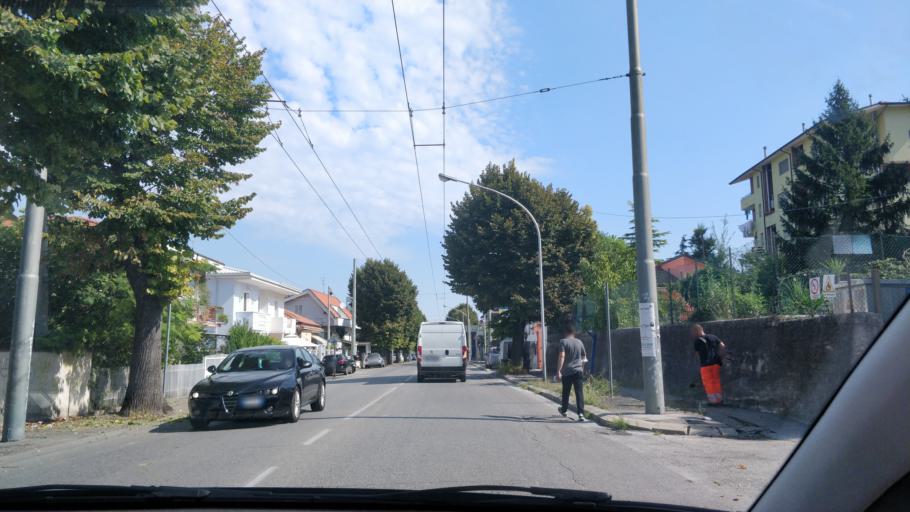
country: IT
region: Abruzzo
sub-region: Provincia di Chieti
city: Chieti
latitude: 42.3811
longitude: 14.1503
